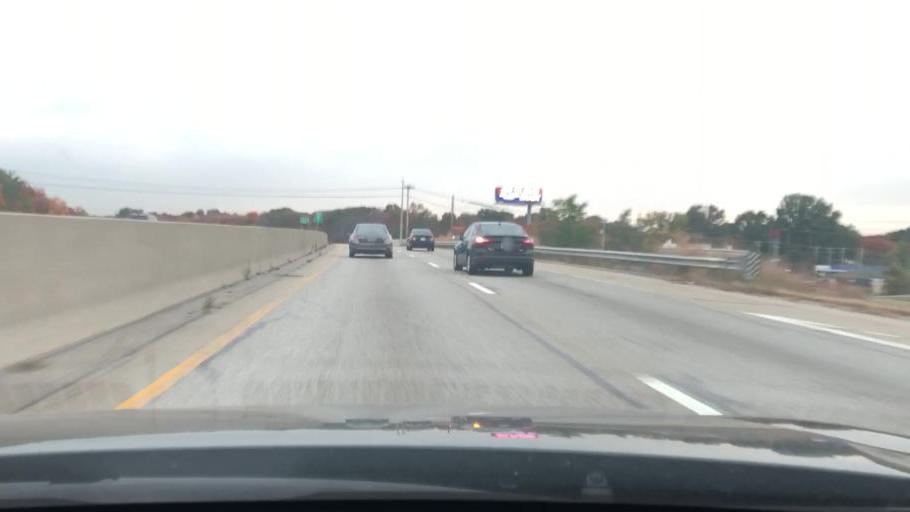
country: US
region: Massachusetts
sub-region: Middlesex County
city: Lowell
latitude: 42.6123
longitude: -71.3276
